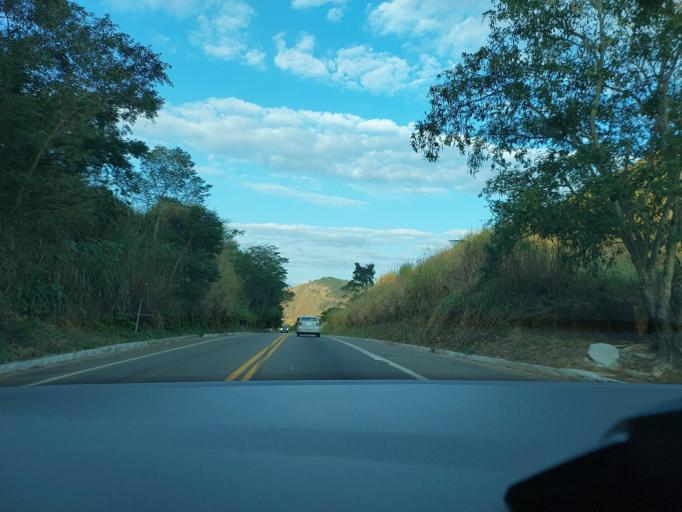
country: BR
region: Minas Gerais
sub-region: Muriae
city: Muriae
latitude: -21.1261
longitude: -42.2504
